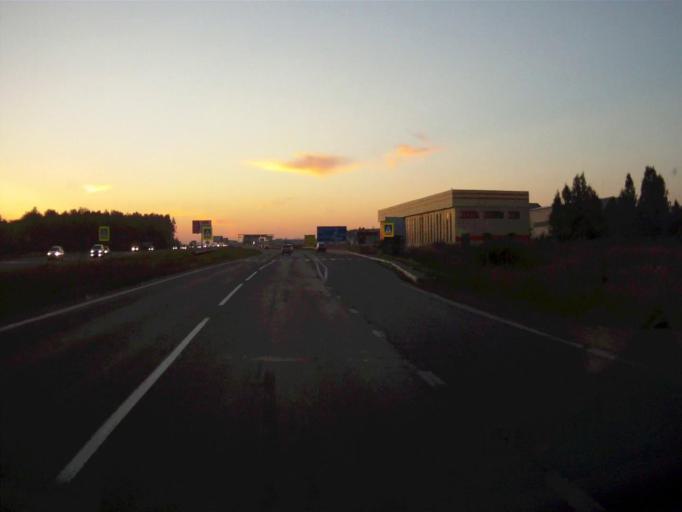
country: RU
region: Chelyabinsk
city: Roshchino
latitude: 55.1824
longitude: 61.2481
